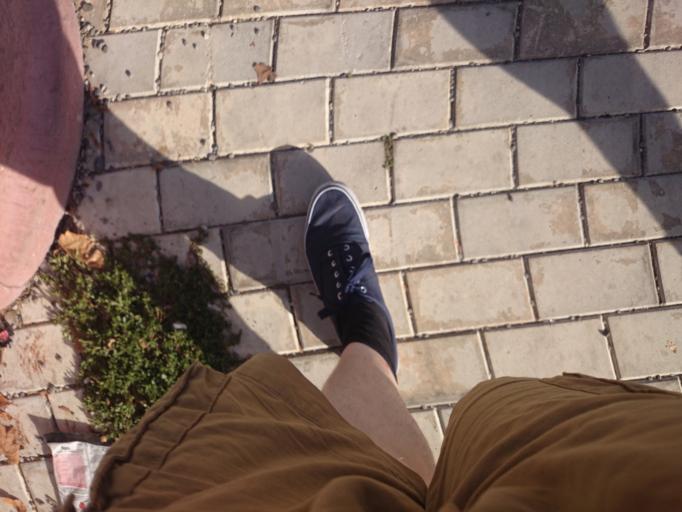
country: ME
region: Kotor
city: Kotor
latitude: 42.4358
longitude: 18.7653
